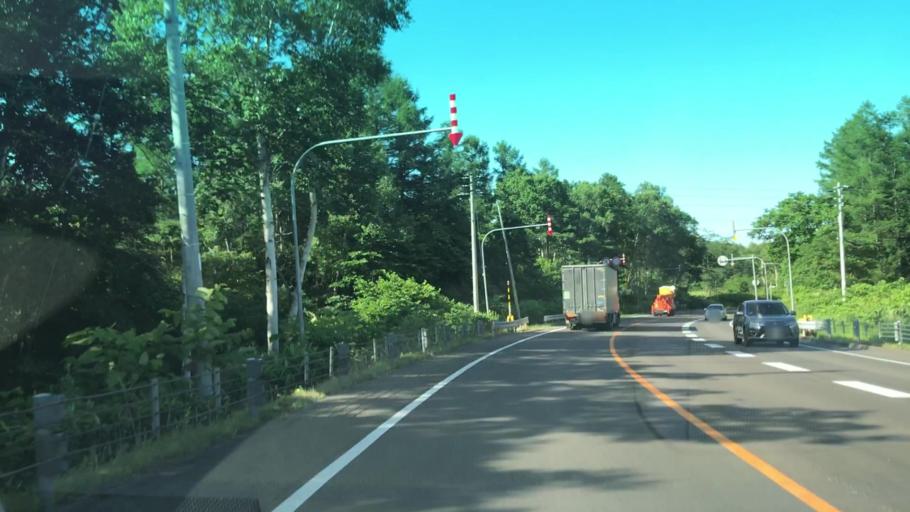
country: JP
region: Hokkaido
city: Yoichi
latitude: 43.0716
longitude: 140.6992
